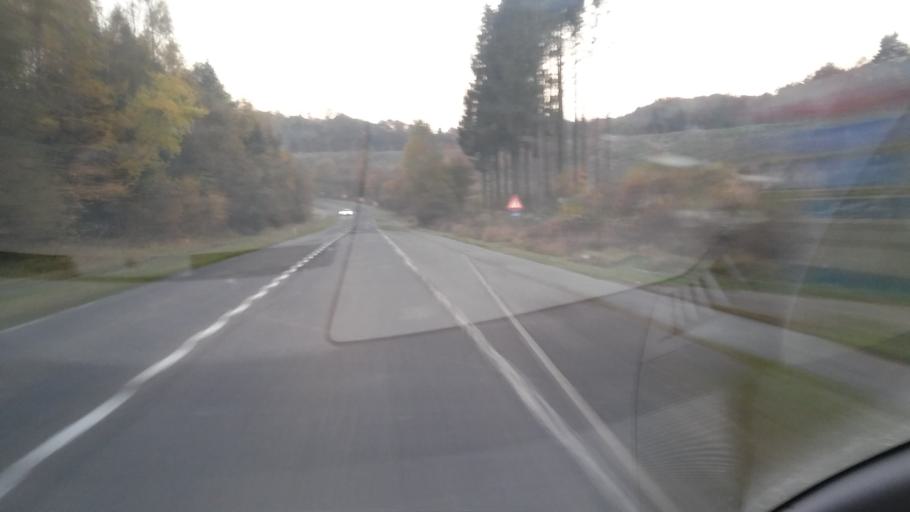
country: BE
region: Wallonia
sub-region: Province du Luxembourg
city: Etalle
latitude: 49.6439
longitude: 5.5714
